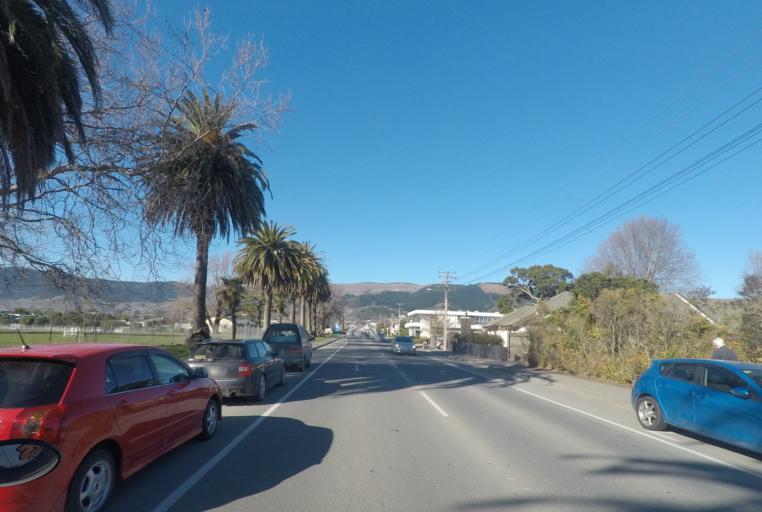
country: NZ
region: Tasman
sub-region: Tasman District
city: Richmond
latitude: -41.3340
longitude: 173.1789
